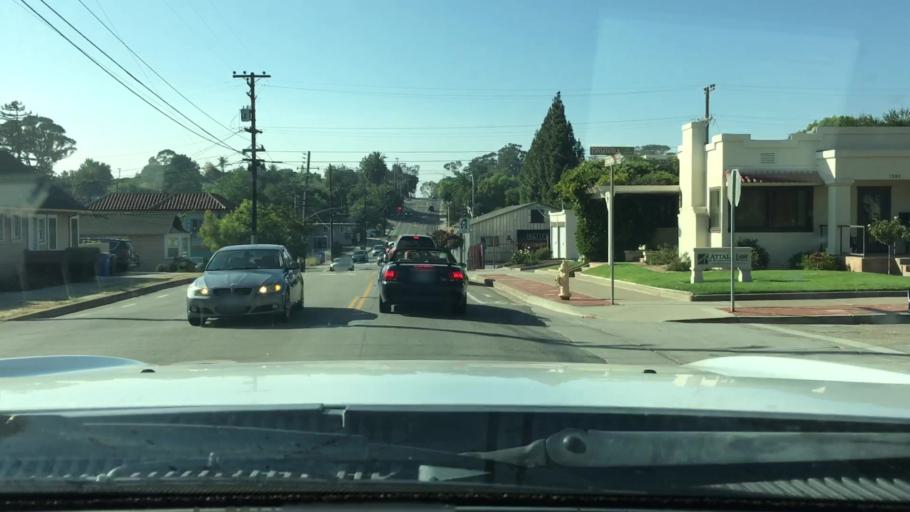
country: US
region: California
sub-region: San Luis Obispo County
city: San Luis Obispo
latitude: 35.2853
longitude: -120.6539
